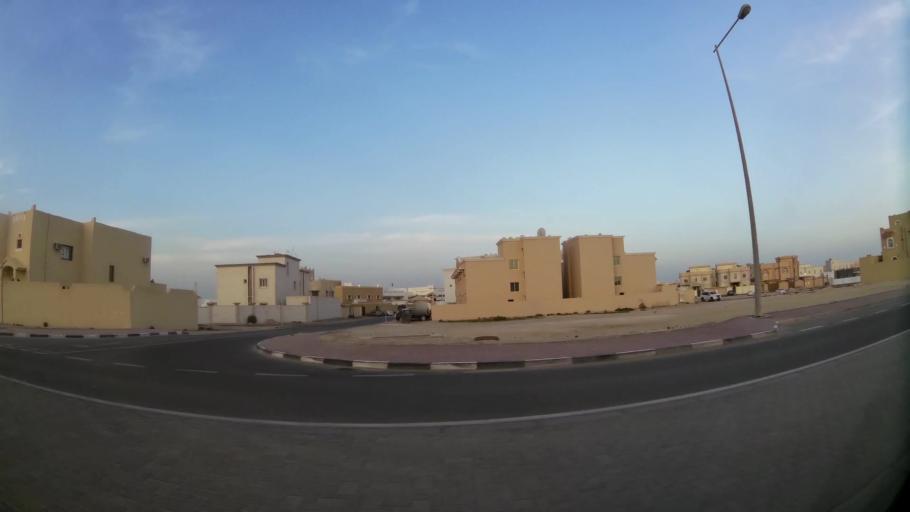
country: QA
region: Al Wakrah
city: Al Wakrah
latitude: 25.1867
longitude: 51.6080
